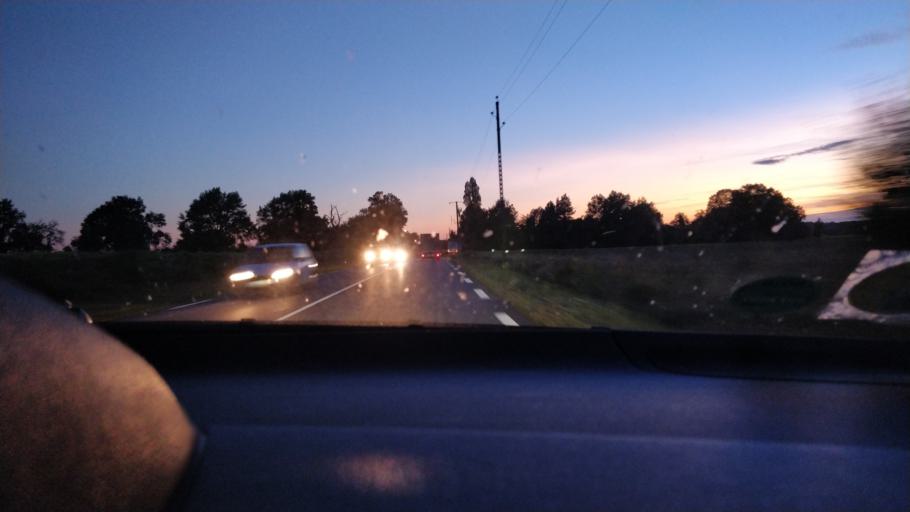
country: FR
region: Poitou-Charentes
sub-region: Departement de la Charente
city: Saint-Claud
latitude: 45.8604
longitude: 0.5237
